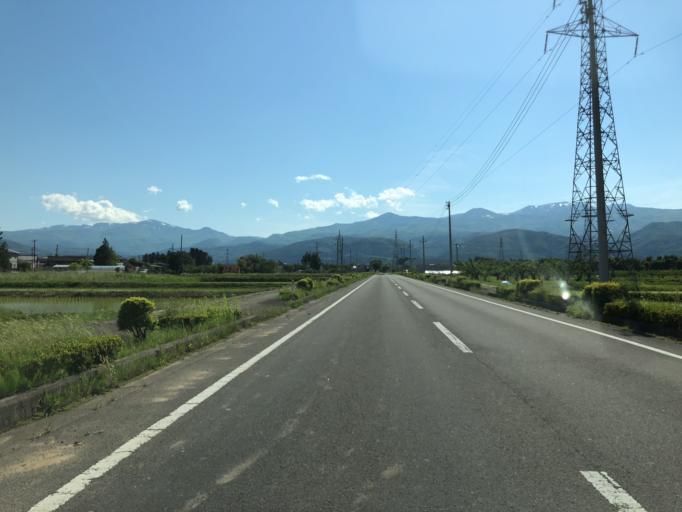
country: JP
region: Fukushima
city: Fukushima-shi
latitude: 37.7532
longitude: 140.4005
